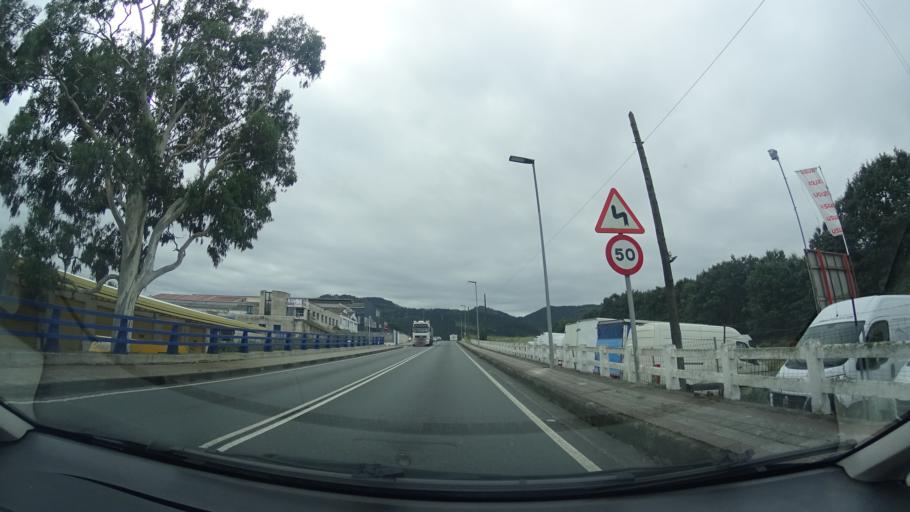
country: ES
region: Basque Country
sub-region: Bizkaia
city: Galdakao
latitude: 43.2134
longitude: -2.8111
